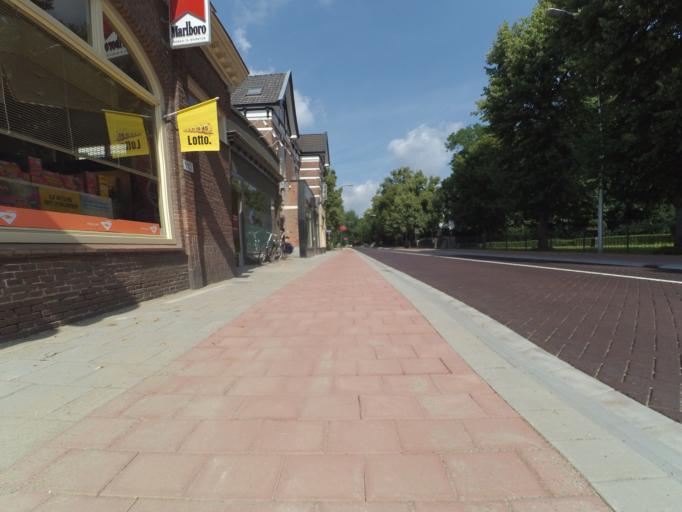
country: NL
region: Utrecht
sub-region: Gemeente Utrechtse Heuvelrug
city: Driebergen-Rijsenburg
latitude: 52.0562
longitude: 5.2756
